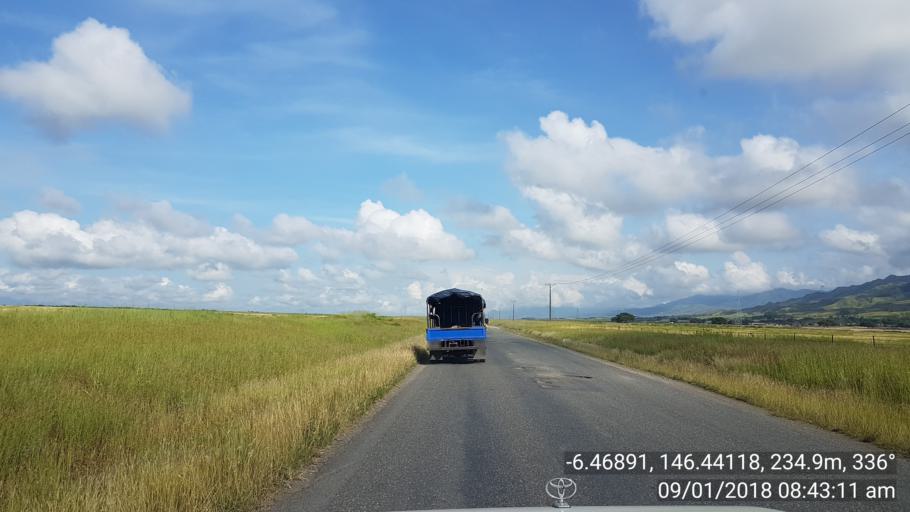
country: PG
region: Morobe
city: Lae
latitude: -6.4689
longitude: 146.4411
